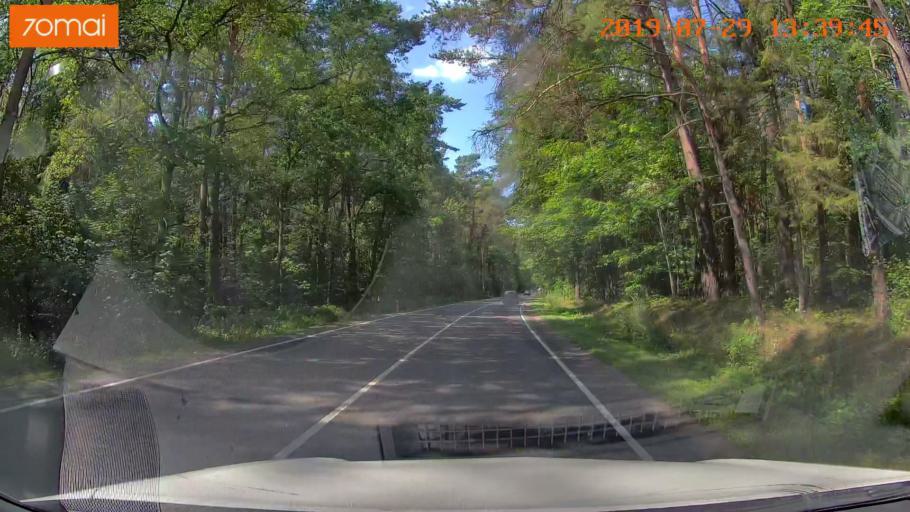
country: RU
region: Kaliningrad
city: Svetlyy
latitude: 54.7247
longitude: 20.1479
